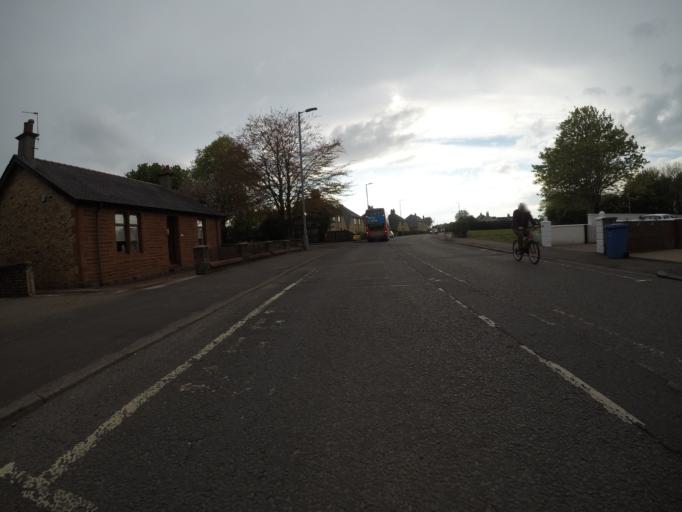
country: GB
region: Scotland
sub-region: North Ayrshire
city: Dreghorn
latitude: 55.6068
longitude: -4.6235
